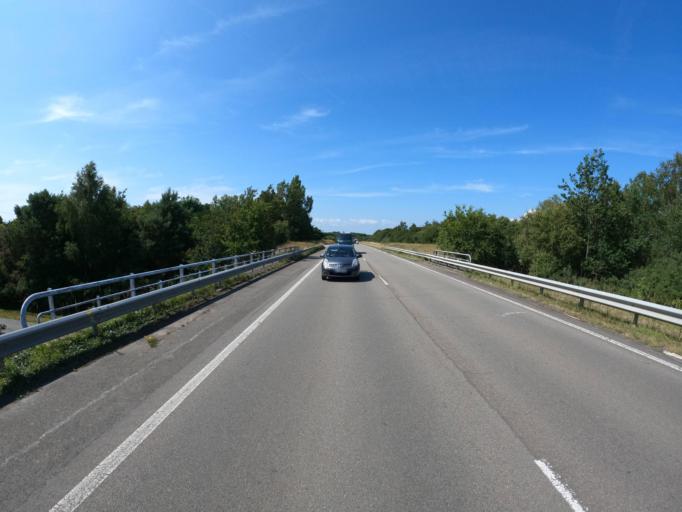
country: FR
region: Pays de la Loire
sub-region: Departement de la Loire-Atlantique
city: La Bernerie-en-Retz
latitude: 47.0955
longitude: -2.0360
